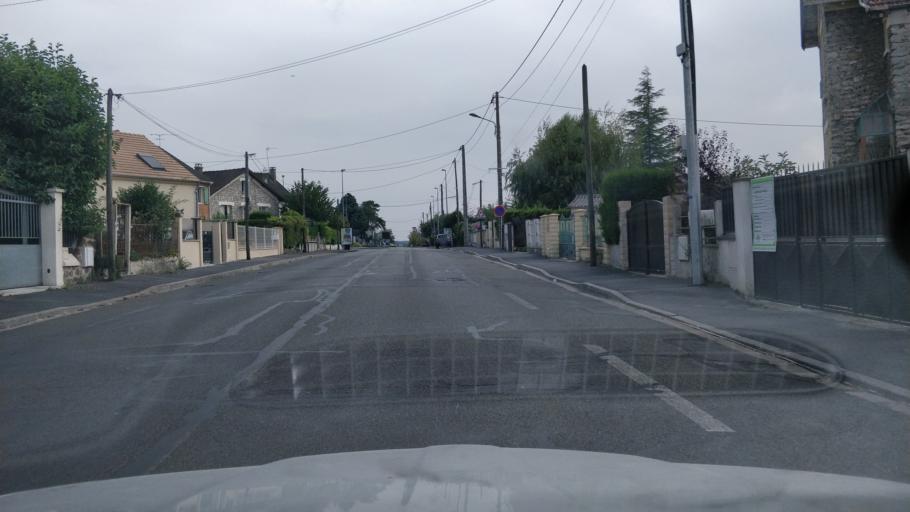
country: FR
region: Ile-de-France
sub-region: Departement de Seine-et-Marne
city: Thorigny-sur-Marne
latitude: 48.8915
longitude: 2.7069
